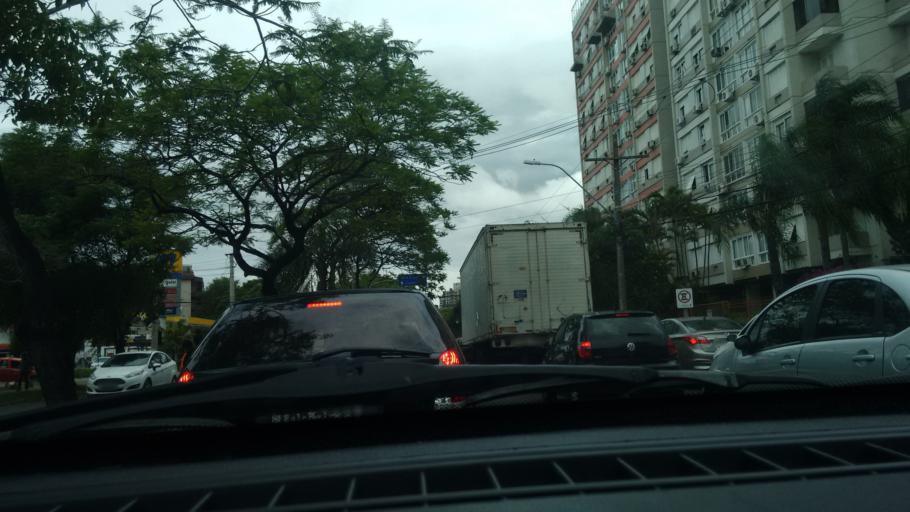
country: BR
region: Rio Grande do Sul
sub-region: Porto Alegre
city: Porto Alegre
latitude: -30.0341
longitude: -51.1850
